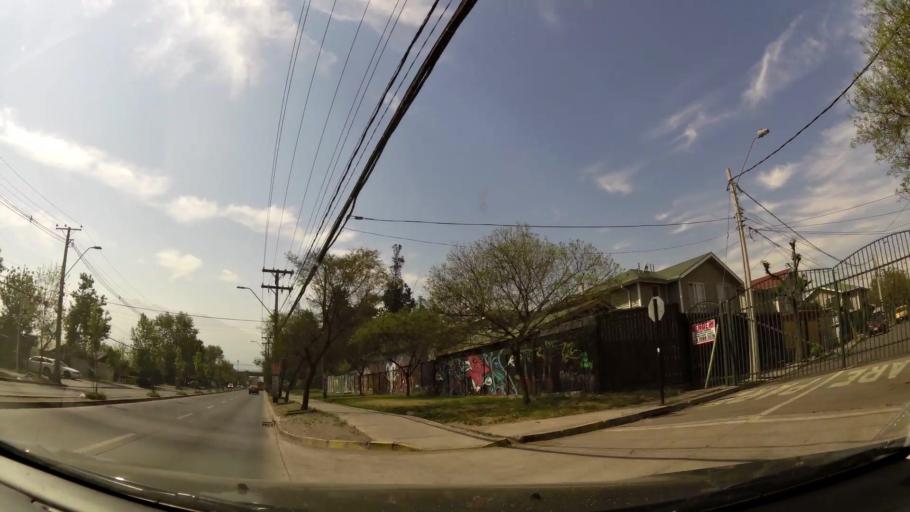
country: CL
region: Santiago Metropolitan
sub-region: Provincia de Cordillera
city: Puente Alto
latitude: -33.5797
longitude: -70.5843
